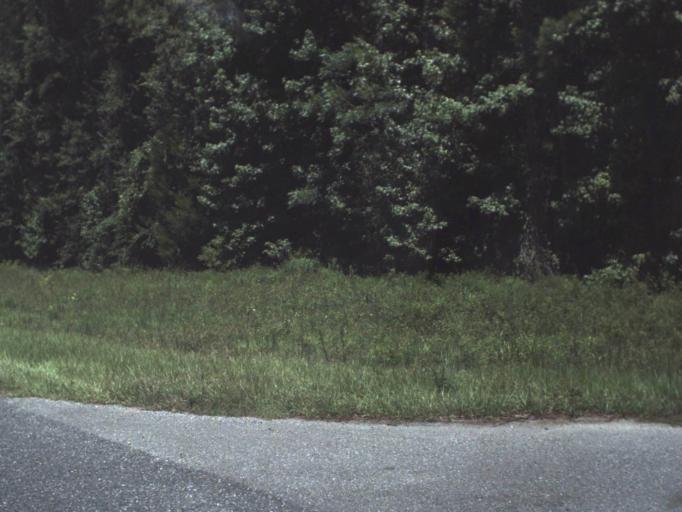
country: US
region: Florida
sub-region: Taylor County
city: Perry
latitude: 30.2778
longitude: -83.7249
